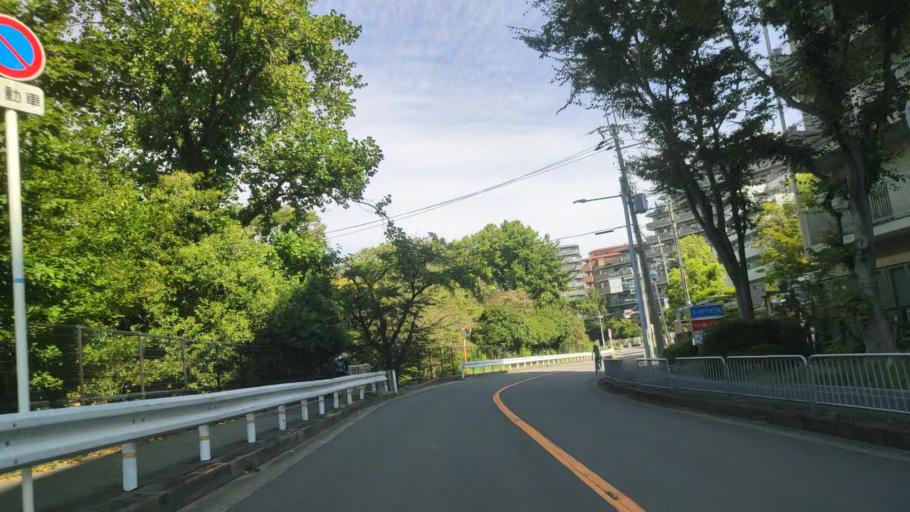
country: JP
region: Osaka
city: Mino
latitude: 34.8240
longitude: 135.5171
